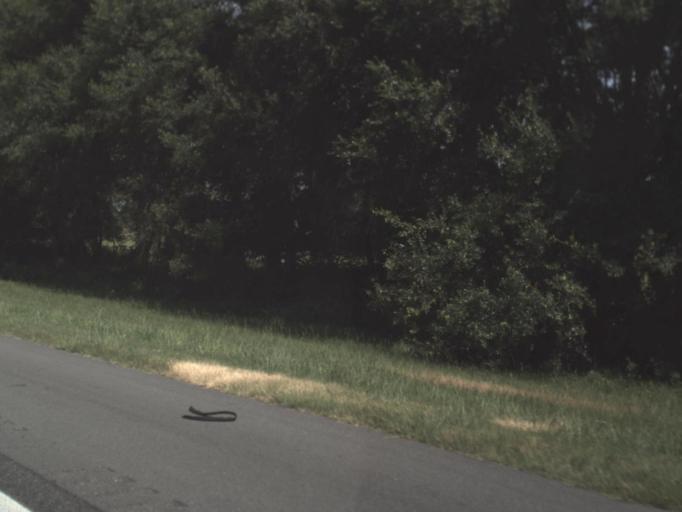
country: US
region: Florida
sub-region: Madison County
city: Madison
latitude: 30.3770
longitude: -83.2844
